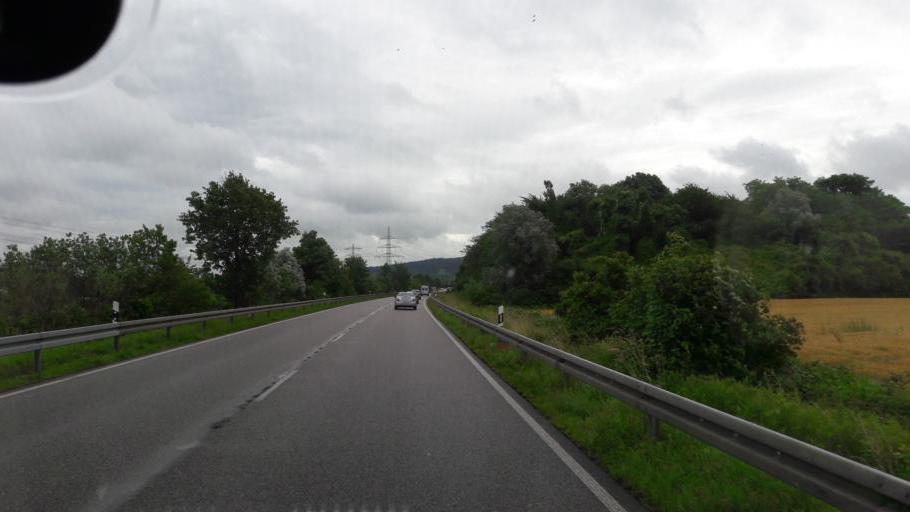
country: DE
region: Baden-Wuerttemberg
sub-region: Karlsruhe Region
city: Ettlingen
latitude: 48.9579
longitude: 8.3968
